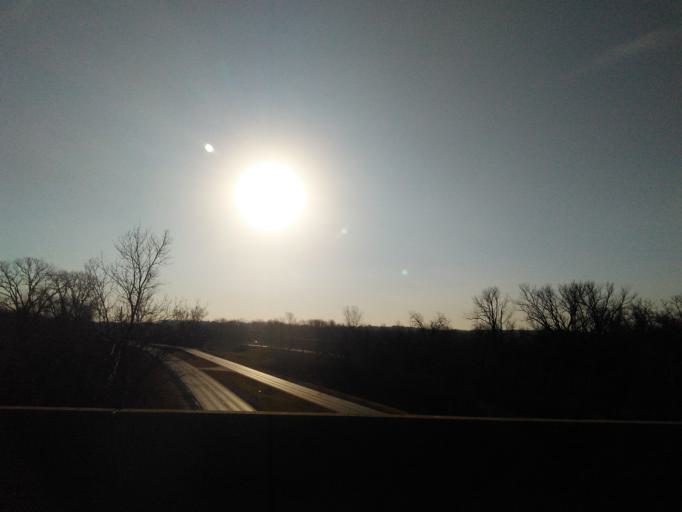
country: US
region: Illinois
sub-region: Saint Clair County
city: Washington Park
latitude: 38.6093
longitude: -90.0808
